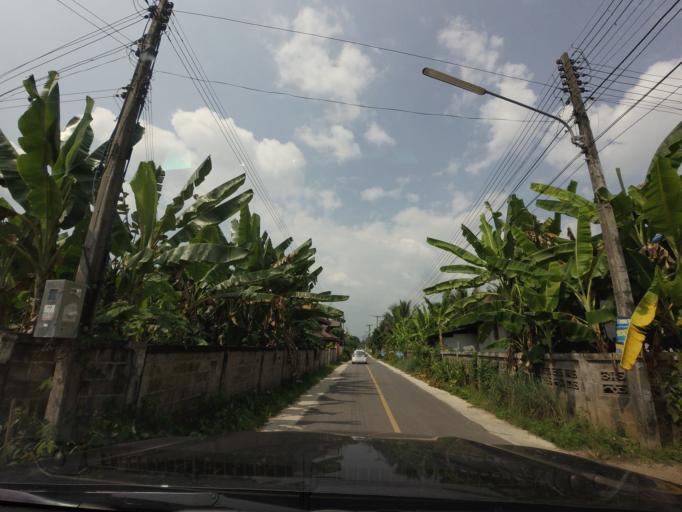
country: TH
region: Nan
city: Pua
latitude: 19.1698
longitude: 100.9382
